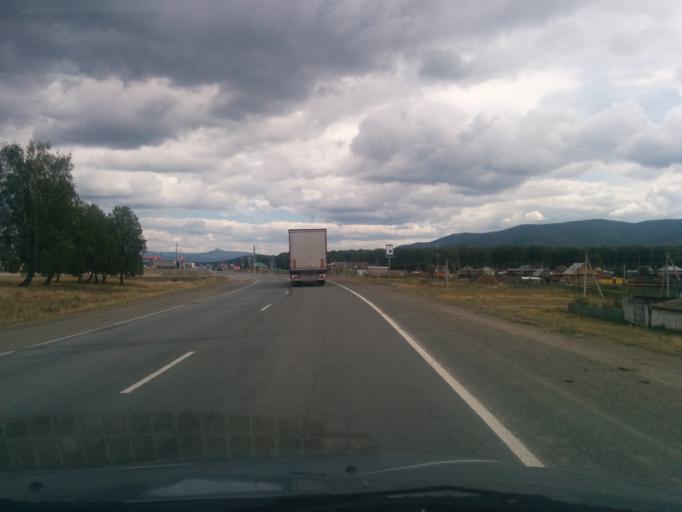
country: RU
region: Bashkortostan
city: Lomovka
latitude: 53.8834
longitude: 58.1005
